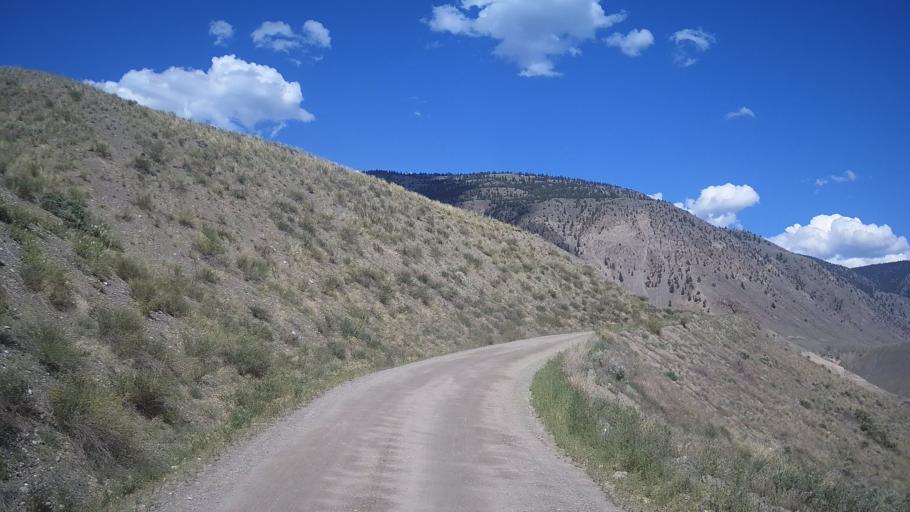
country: CA
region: British Columbia
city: Lillooet
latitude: 51.1834
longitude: -122.1176
